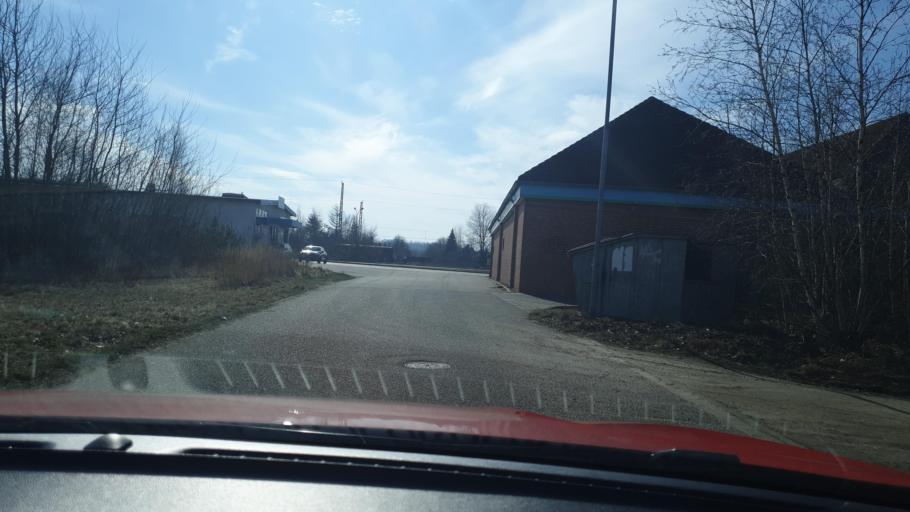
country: DE
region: Saxony
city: Ossling
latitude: 51.4442
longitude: 14.1373
